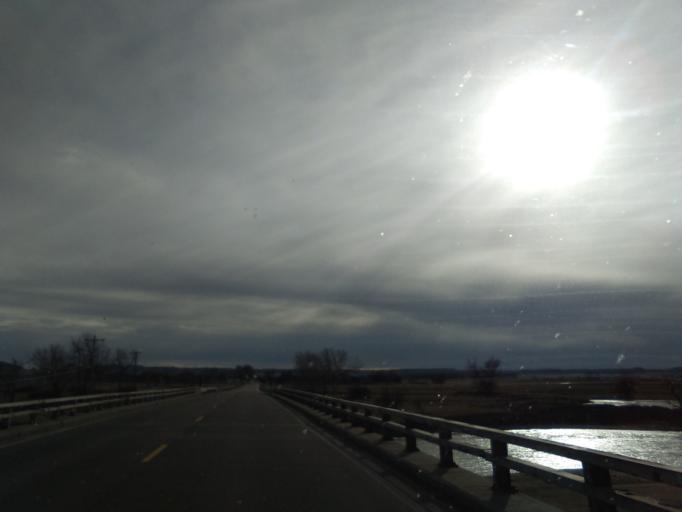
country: US
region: Nebraska
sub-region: Scotts Bluff County
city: Gering
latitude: 41.7898
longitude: -103.5191
